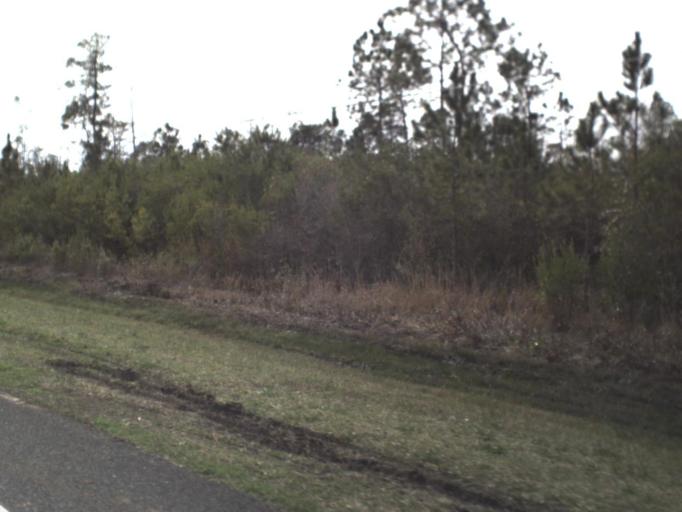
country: US
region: Florida
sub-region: Bay County
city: Youngstown
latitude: 30.5011
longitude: -85.4141
